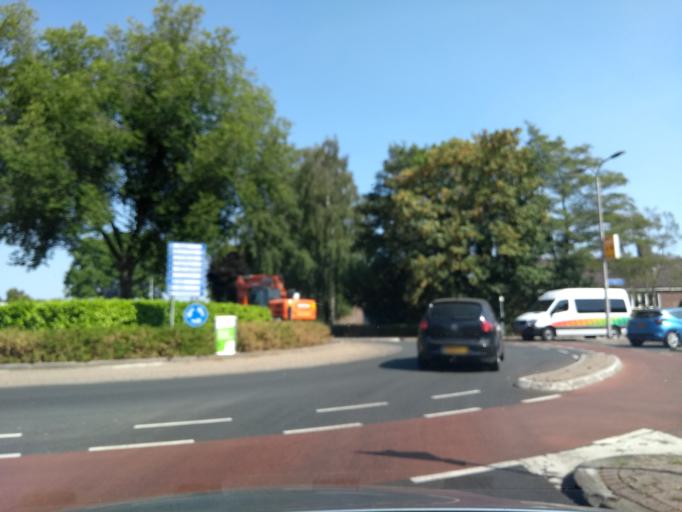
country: NL
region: Overijssel
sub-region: Gemeente Twenterand
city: Vroomshoop
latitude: 52.4615
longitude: 6.5659
